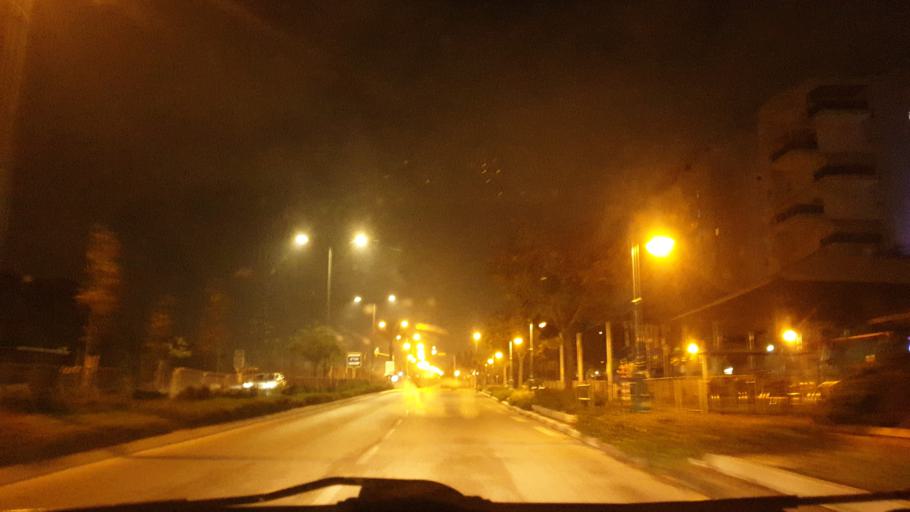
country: IL
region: Central District
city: Bet Dagan
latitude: 31.9743
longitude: 34.8161
